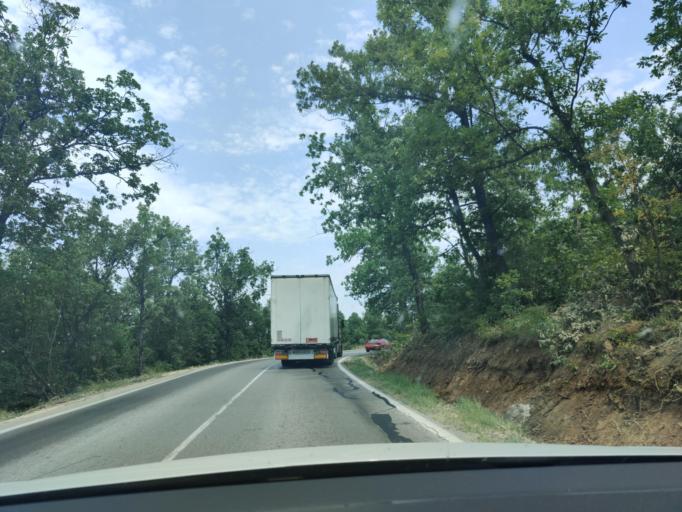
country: BG
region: Vidin
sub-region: Obshtina Dimovo
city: Dimovo
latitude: 43.6764
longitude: 22.7717
